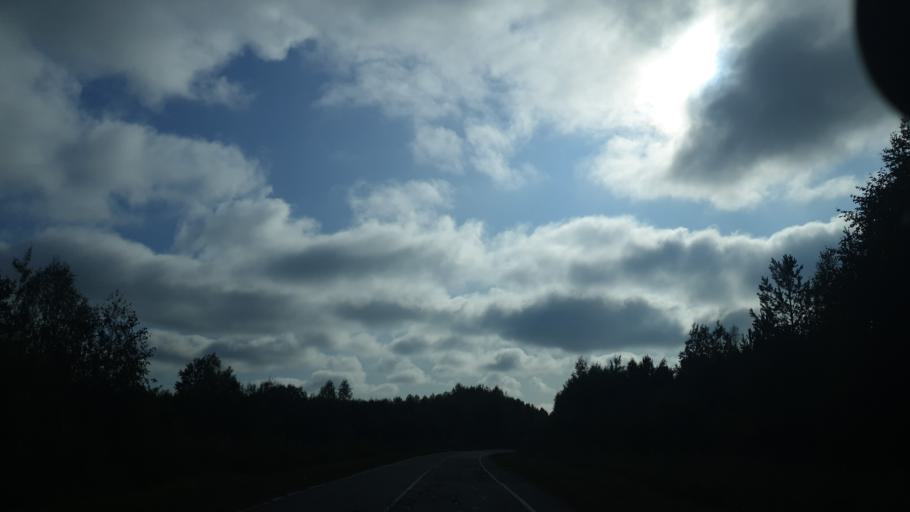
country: RU
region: Komi Republic
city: Vizinga
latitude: 60.6096
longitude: 50.4259
